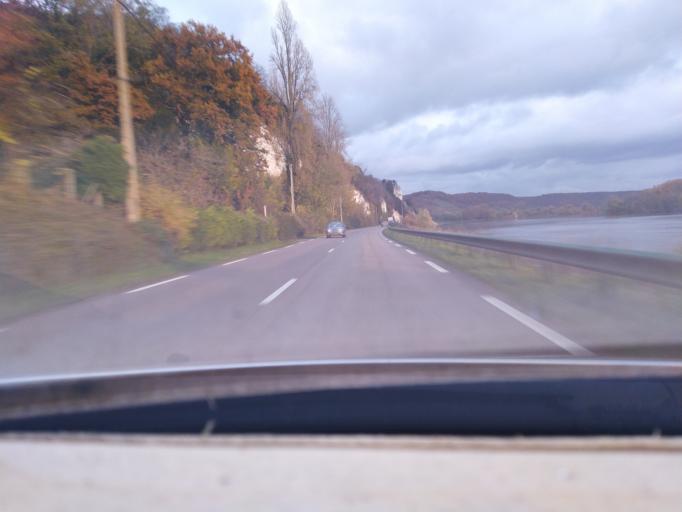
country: FR
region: Haute-Normandie
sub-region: Departement de la Seine-Maritime
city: Saint-Pierre-de-Varengeville
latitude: 49.4864
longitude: 0.9062
